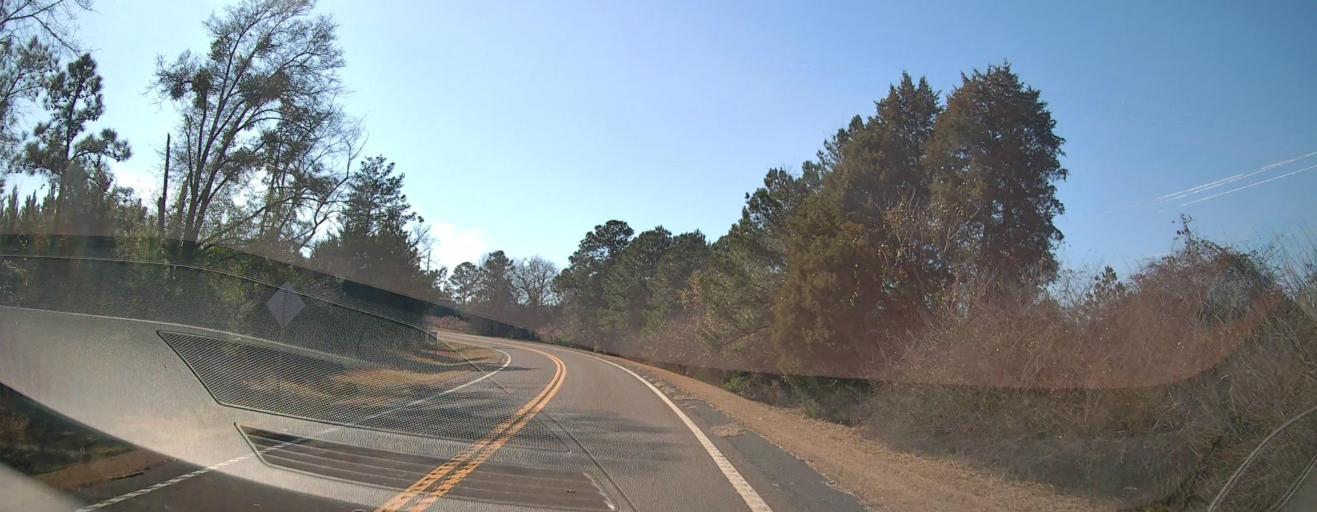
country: US
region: Georgia
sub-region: Macon County
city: Oglethorpe
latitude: 32.1966
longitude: -84.1538
